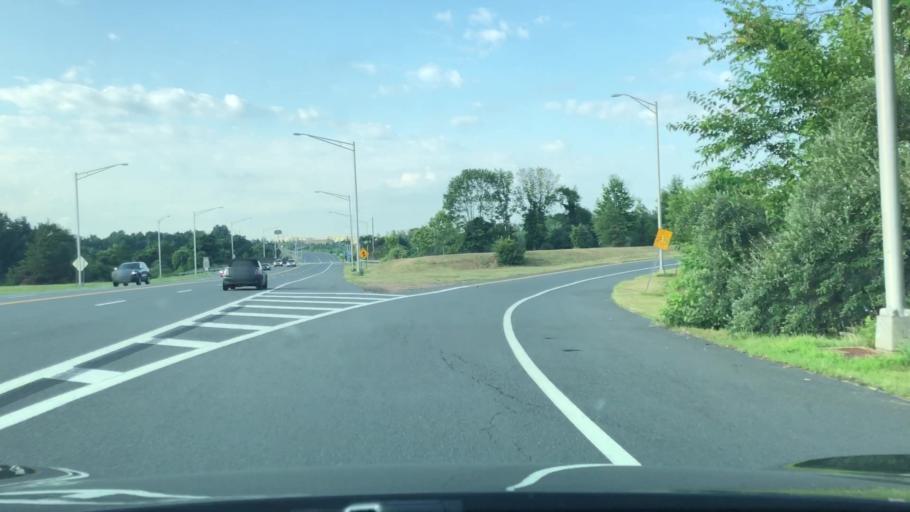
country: US
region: New Jersey
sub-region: Mercer County
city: Ewing
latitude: 40.2921
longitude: -74.8112
